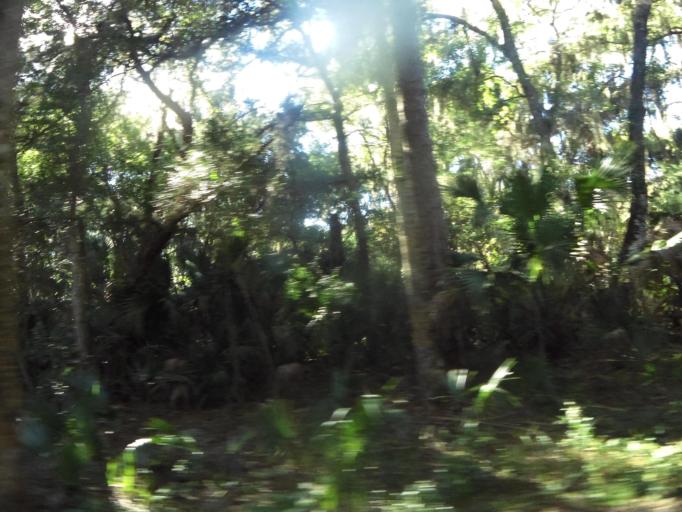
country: US
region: Florida
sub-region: Duval County
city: Atlantic Beach
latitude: 30.4120
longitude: -81.4315
